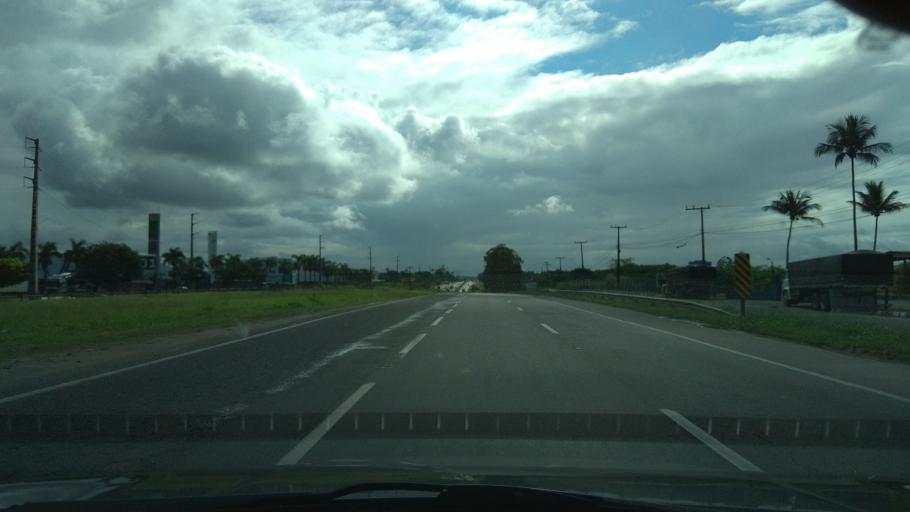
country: BR
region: Bahia
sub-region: Conceicao Do Jacuipe
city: Conceicao do Jacuipe
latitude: -12.3388
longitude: -38.8472
